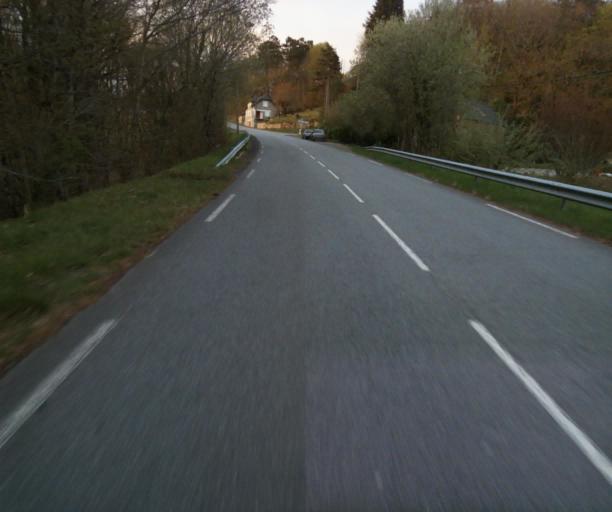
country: FR
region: Limousin
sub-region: Departement de la Correze
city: Laguenne
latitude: 45.2825
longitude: 1.8457
